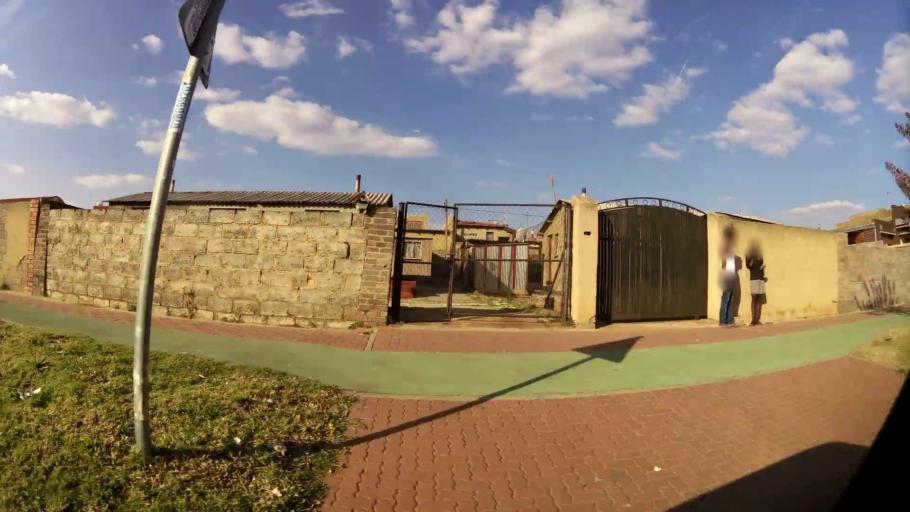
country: ZA
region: Gauteng
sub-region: City of Johannesburg Metropolitan Municipality
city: Roodepoort
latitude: -26.2170
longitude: 27.8856
